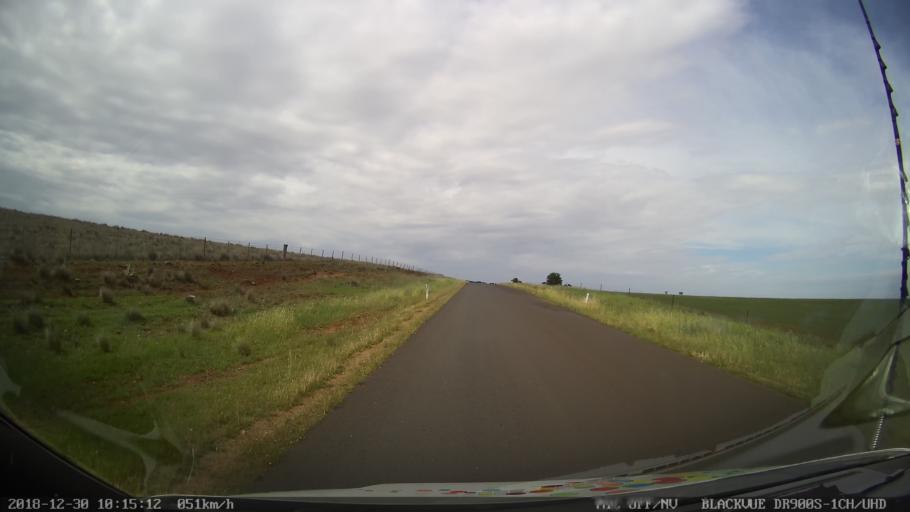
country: AU
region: New South Wales
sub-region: Snowy River
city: Berridale
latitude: -36.5416
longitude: 149.0475
